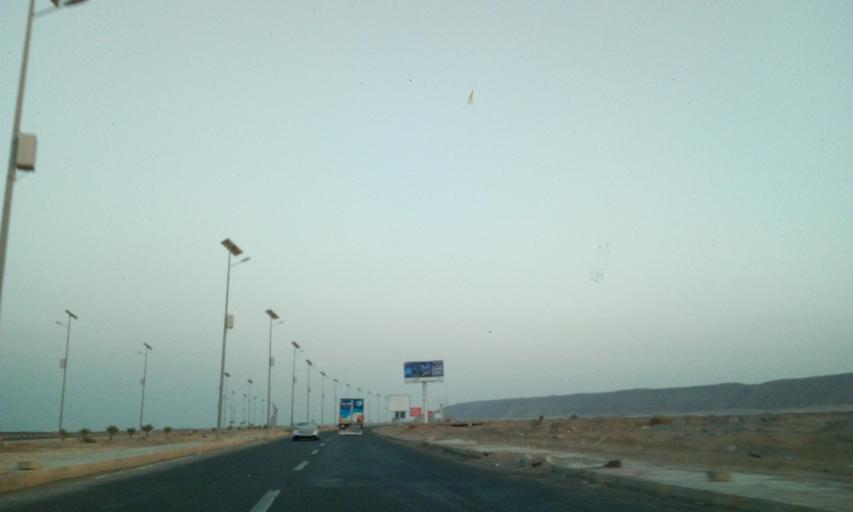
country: EG
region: Red Sea
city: El Gouna
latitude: 27.4154
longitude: 33.6182
